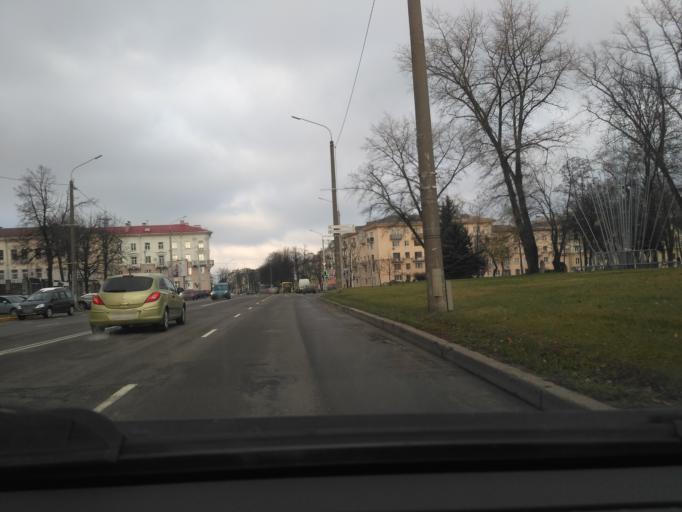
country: BY
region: Minsk
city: Minsk
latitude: 53.9027
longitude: 27.5828
